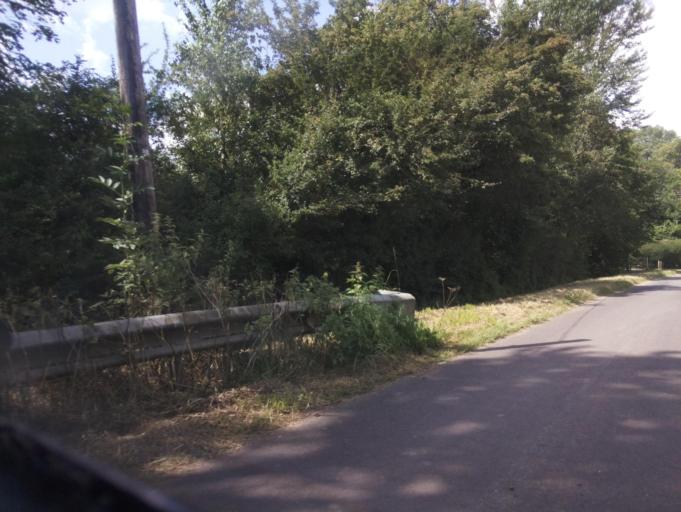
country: GB
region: England
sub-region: Wiltshire
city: Hankerton
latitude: 51.6266
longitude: -2.0279
